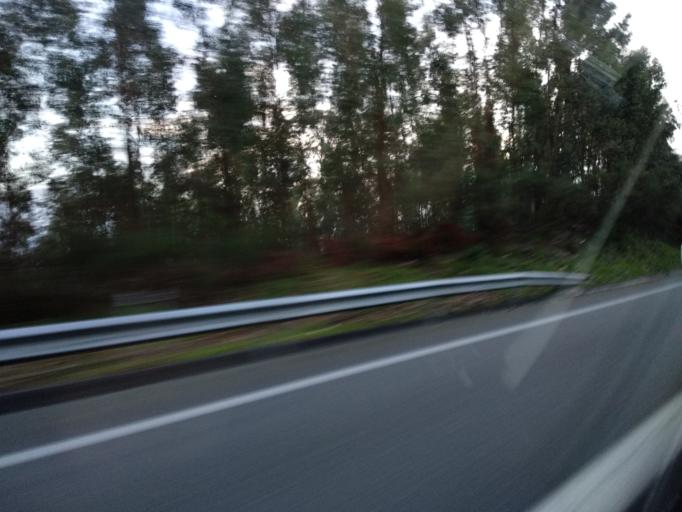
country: PT
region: Braga
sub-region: Braga
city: Oliveira
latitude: 41.4644
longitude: -8.4720
